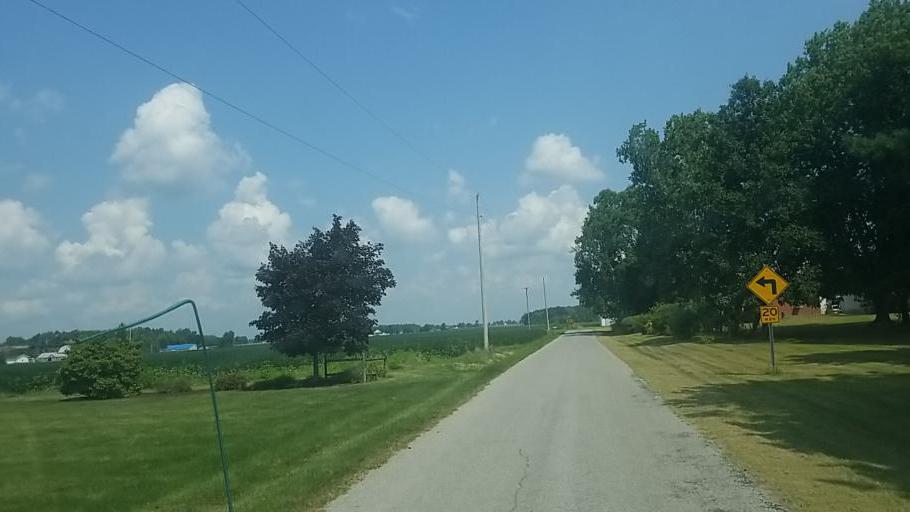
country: US
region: Ohio
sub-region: Crawford County
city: Crestline
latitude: 40.8069
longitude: -82.7259
